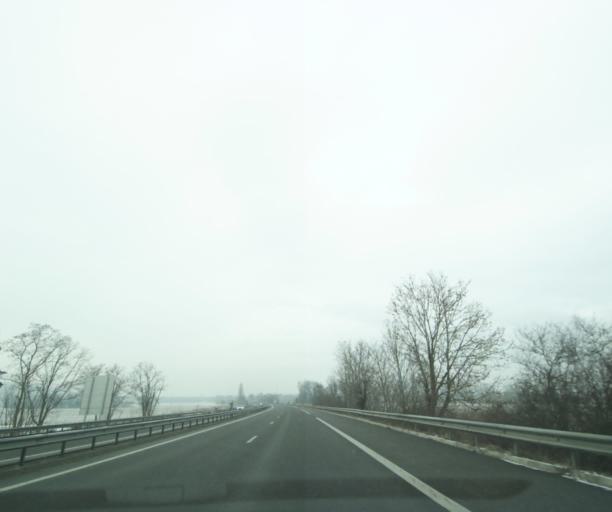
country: FR
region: Auvergne
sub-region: Departement du Puy-de-Dome
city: Culhat
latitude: 45.8391
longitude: 3.3094
